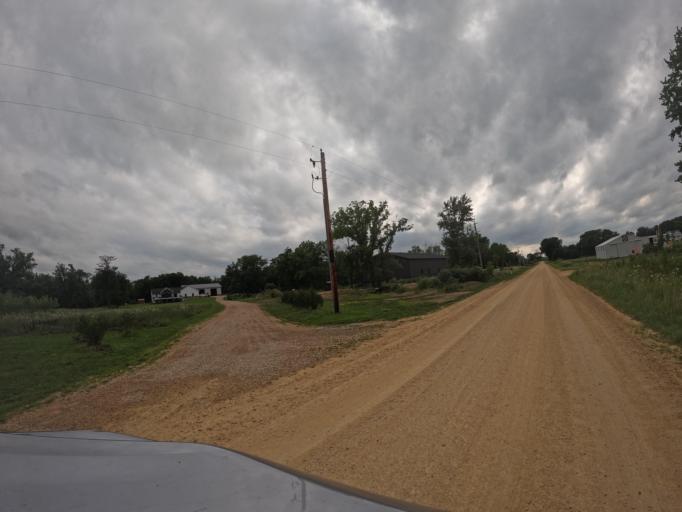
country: US
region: Iowa
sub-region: Clinton County
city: De Witt
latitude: 41.7977
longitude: -90.5580
